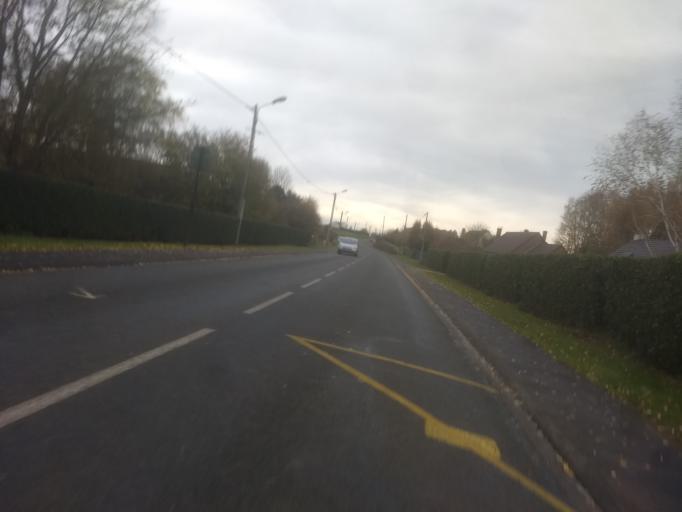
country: FR
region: Nord-Pas-de-Calais
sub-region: Departement du Pas-de-Calais
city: Riviere
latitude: 50.2389
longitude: 2.7087
